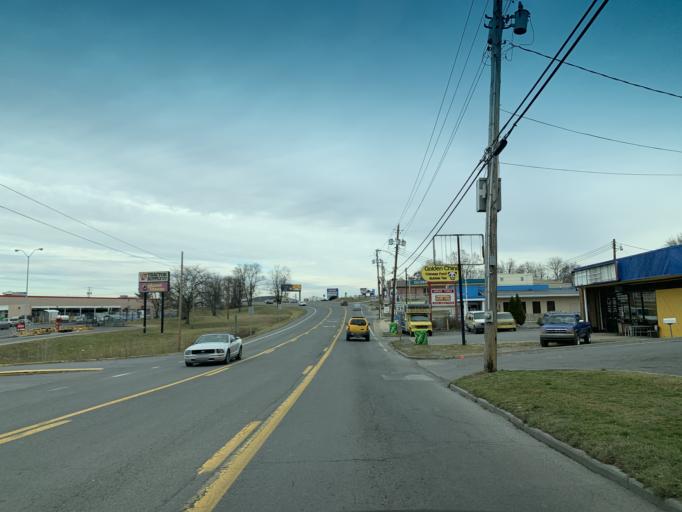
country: US
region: West Virginia
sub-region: Berkeley County
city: Martinsburg
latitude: 39.4700
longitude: -77.9552
